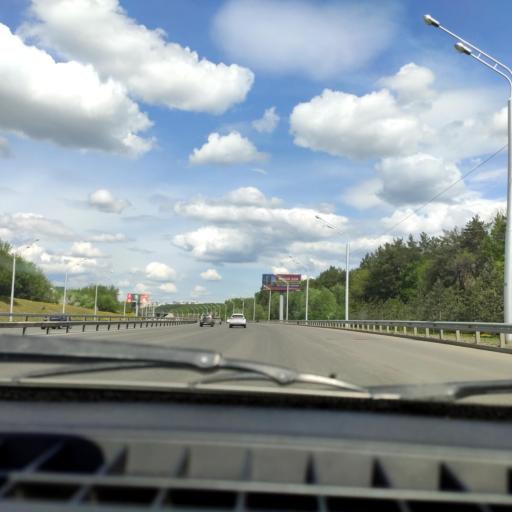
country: RU
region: Bashkortostan
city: Ufa
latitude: 54.7317
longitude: 56.0024
